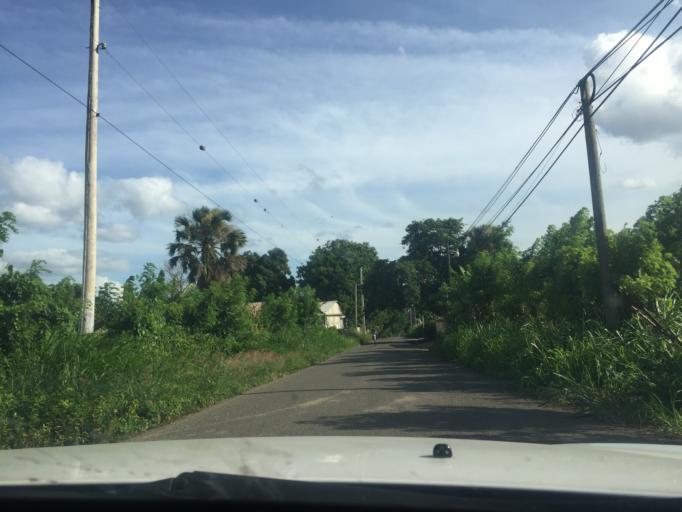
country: DO
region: Santiago
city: Tamboril
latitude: 19.4916
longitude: -70.6357
